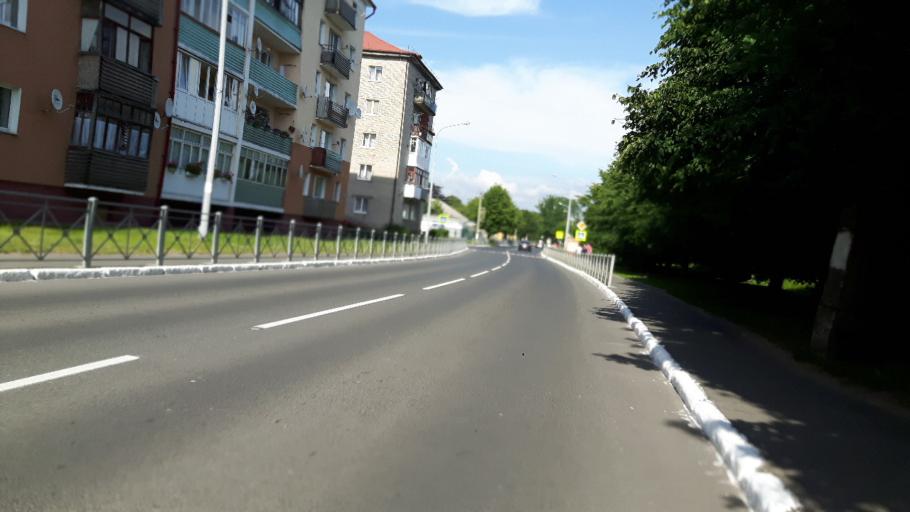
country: RU
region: Kaliningrad
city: Mamonovo
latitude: 54.4606
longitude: 19.9414
